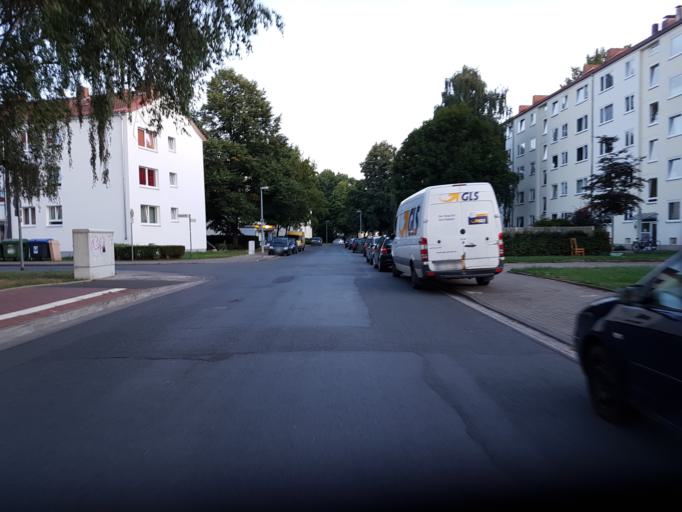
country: DE
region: Lower Saxony
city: Langenhagen
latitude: 52.4134
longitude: 9.7564
